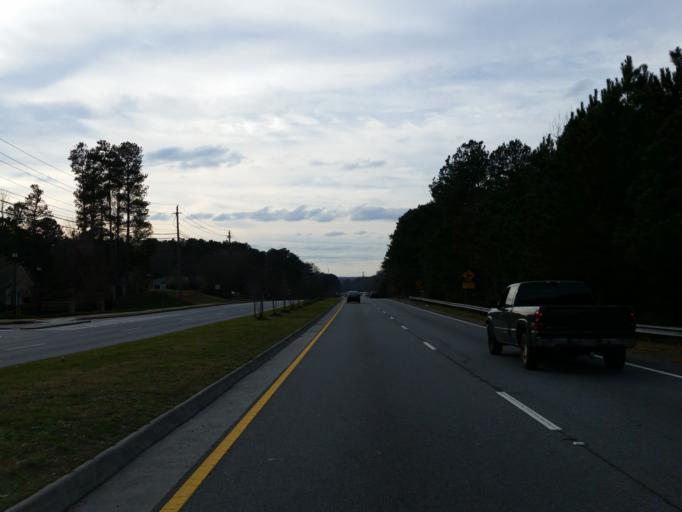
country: US
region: Georgia
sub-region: Cobb County
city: Fair Oaks
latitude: 33.9049
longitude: -84.6084
